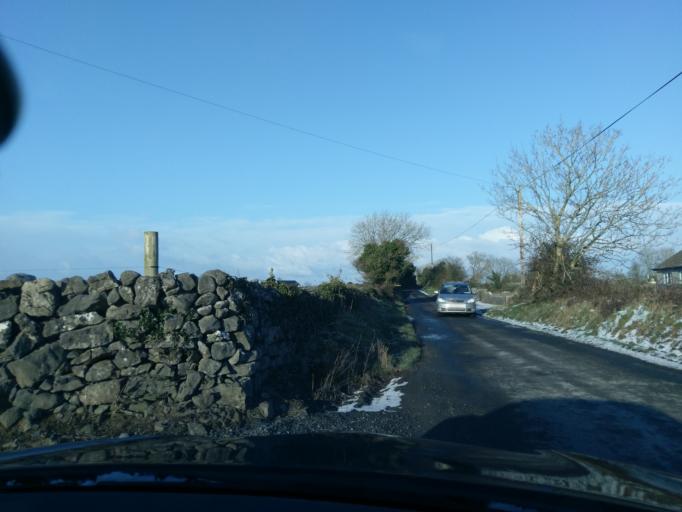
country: IE
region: Connaught
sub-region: County Galway
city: Athenry
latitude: 53.1729
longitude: -8.7478
